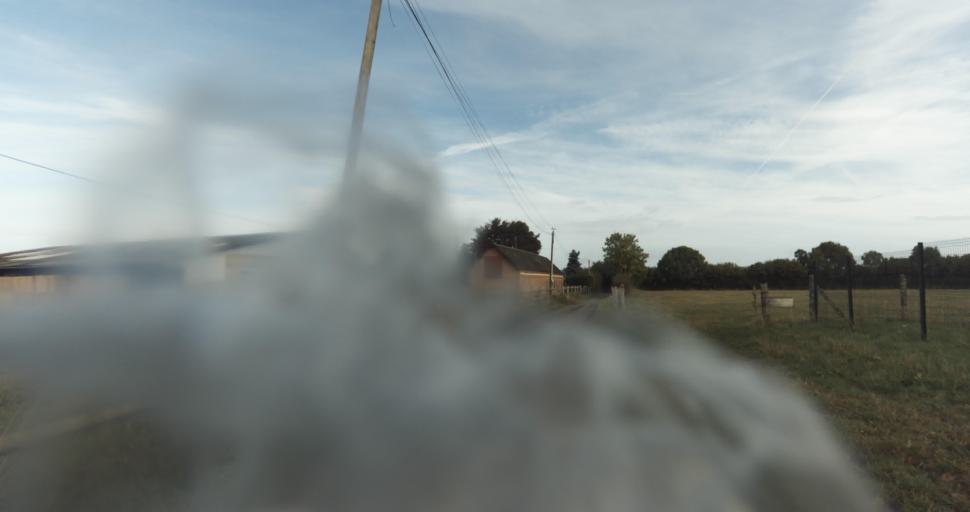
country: FR
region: Lower Normandy
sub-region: Departement de l'Orne
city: Gace
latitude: 48.9023
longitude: 0.3132
